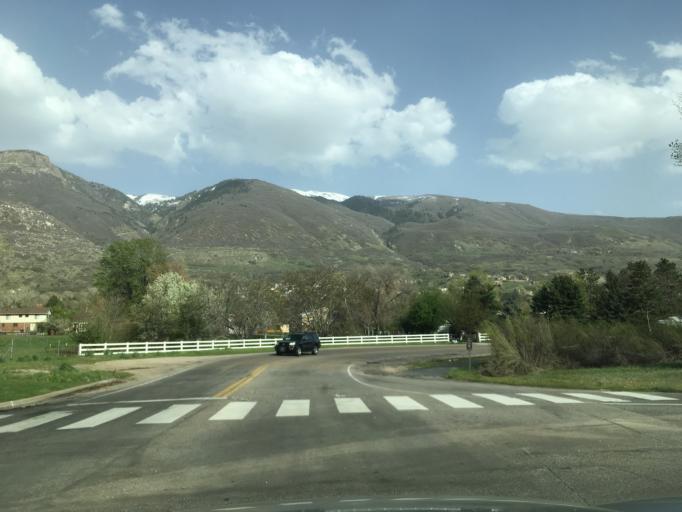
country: US
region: Utah
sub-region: Davis County
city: Farmington
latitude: 40.9734
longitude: -111.8919
